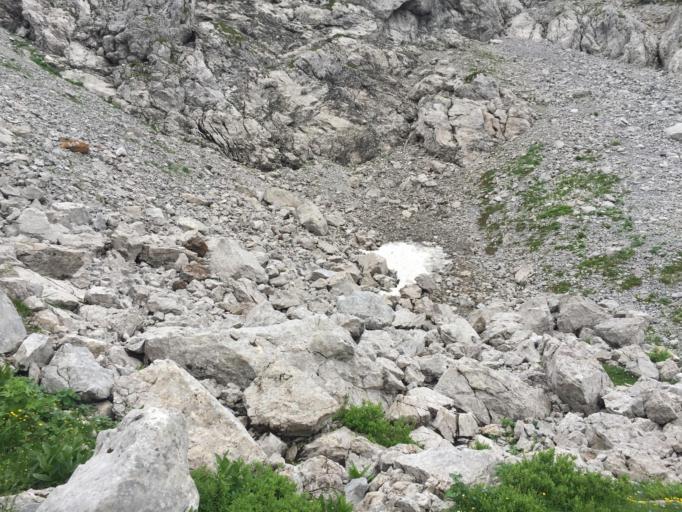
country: IT
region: Friuli Venezia Giulia
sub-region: Provincia di Udine
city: Pontebba
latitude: 46.5567
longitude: 13.2309
